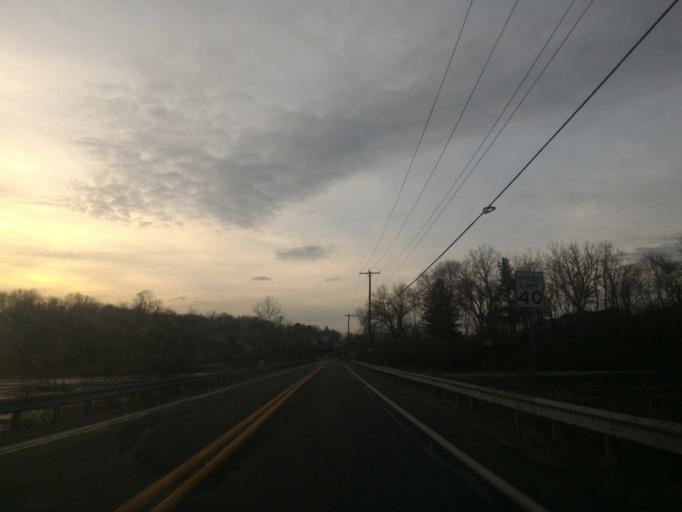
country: US
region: Pennsylvania
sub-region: York County
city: Jacobus
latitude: 39.8858
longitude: -76.6917
